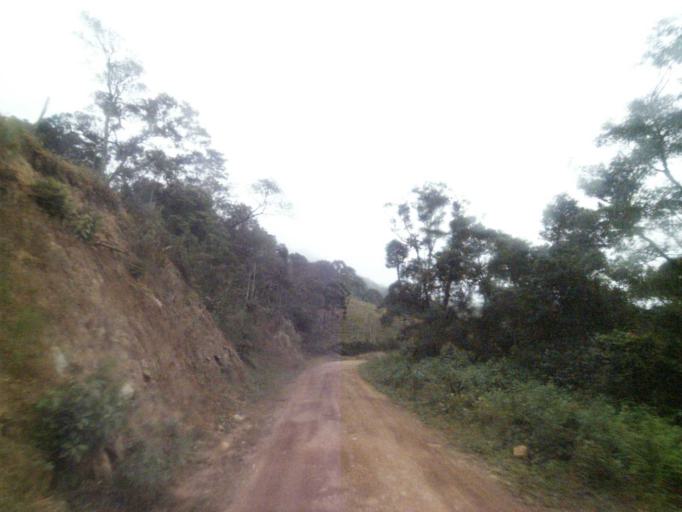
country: BR
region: Santa Catarina
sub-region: Anitapolis
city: Anitapolis
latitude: -27.8562
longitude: -49.1337
